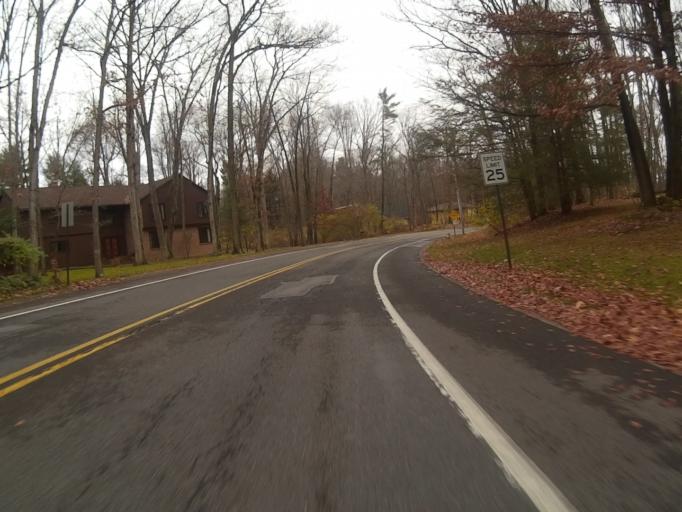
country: US
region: Pennsylvania
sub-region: Centre County
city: Park Forest Village
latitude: 40.8260
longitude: -77.8929
